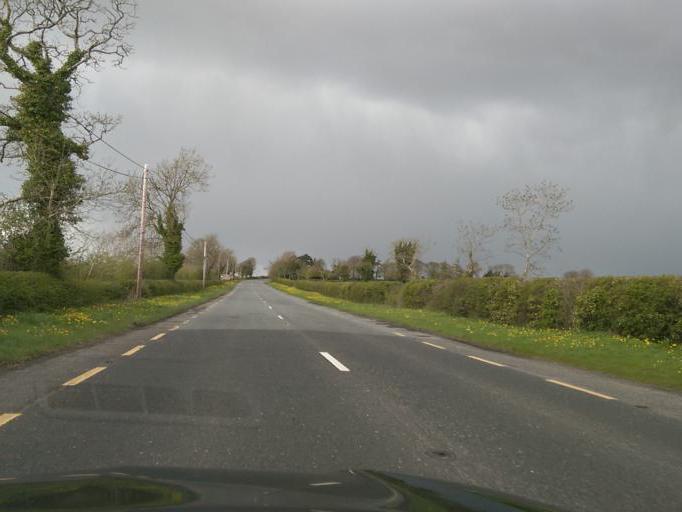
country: IE
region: Leinster
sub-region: An Mhi
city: Dunshaughlin
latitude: 53.5542
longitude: -6.5750
